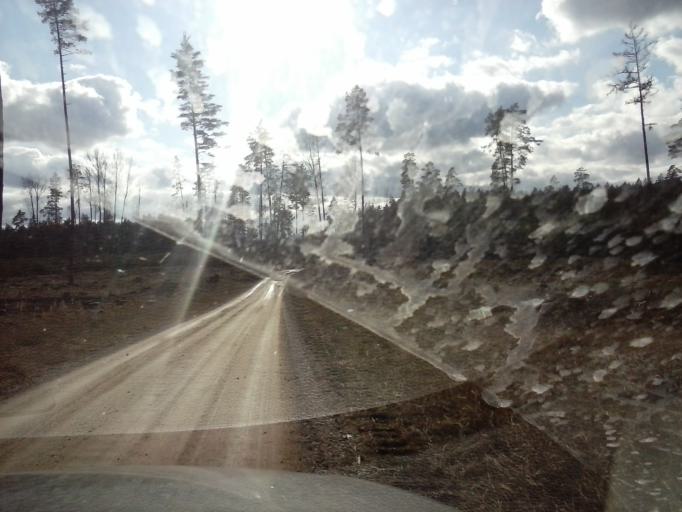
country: EE
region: Valgamaa
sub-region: Torva linn
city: Torva
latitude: 58.1557
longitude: 26.1386
